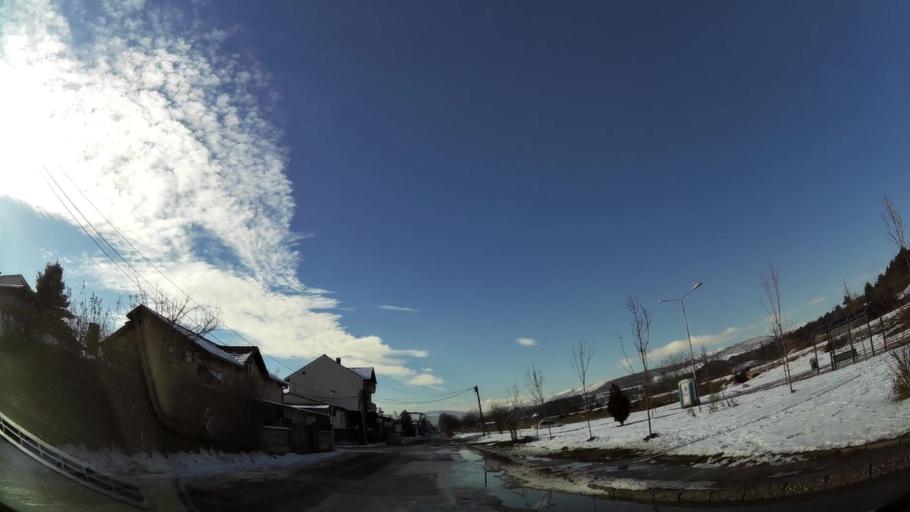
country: MK
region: Saraj
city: Saraj
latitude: 42.0103
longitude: 21.3402
